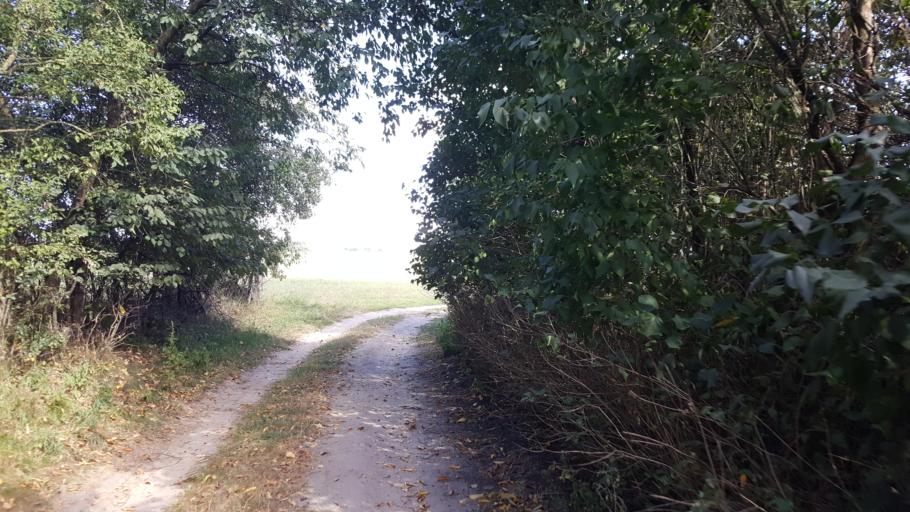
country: BY
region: Brest
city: Vysokaye
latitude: 52.2756
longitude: 23.4984
